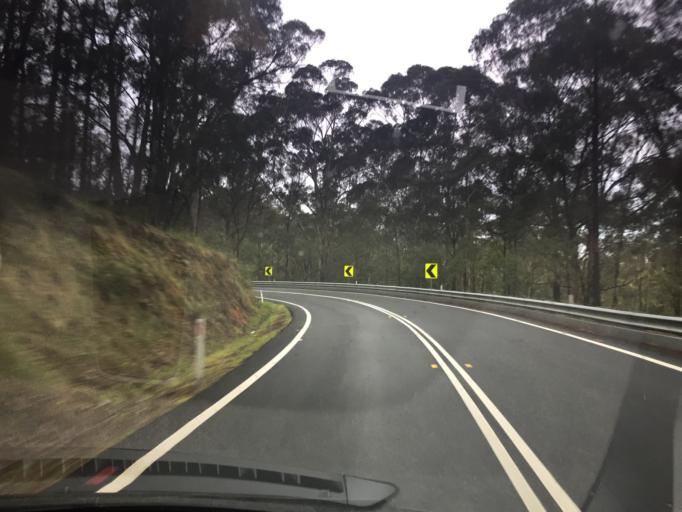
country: AU
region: New South Wales
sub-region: Bega Valley
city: Bega
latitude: -36.6100
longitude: 149.4818
